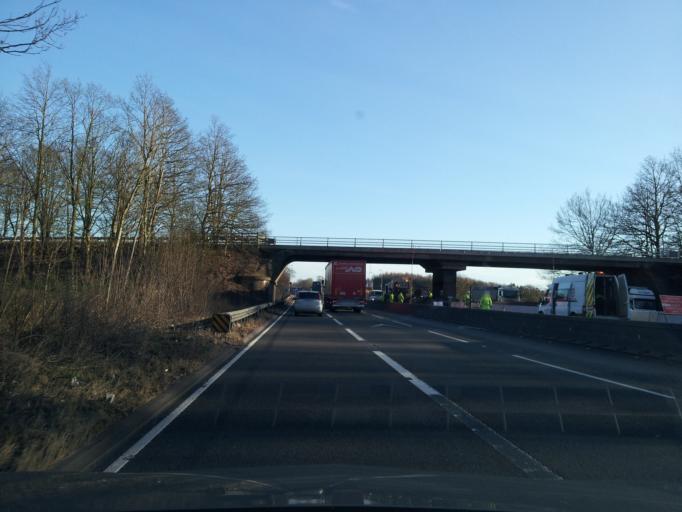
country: GB
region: England
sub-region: Northamptonshire
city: Long Buckby
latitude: 52.2531
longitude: -1.0742
